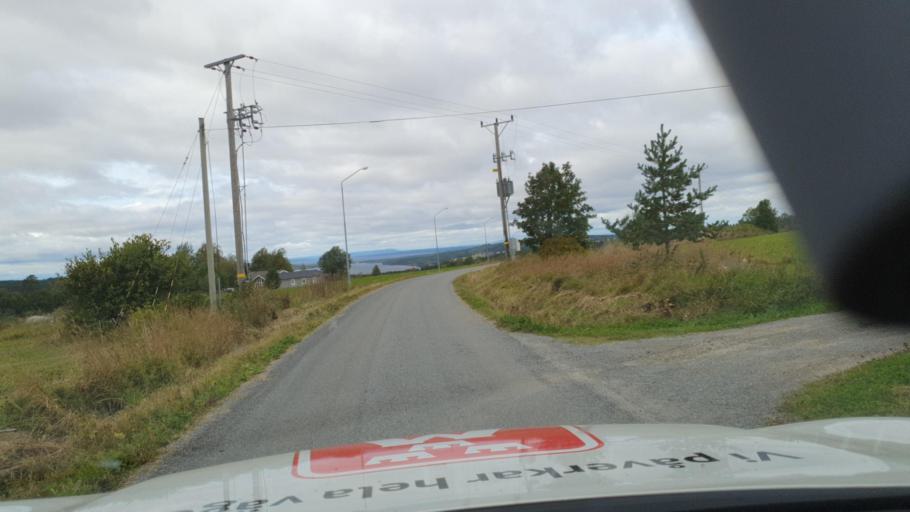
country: SE
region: Jaemtland
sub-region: OEstersunds Kommun
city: Ostersund
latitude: 63.1316
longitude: 14.5770
